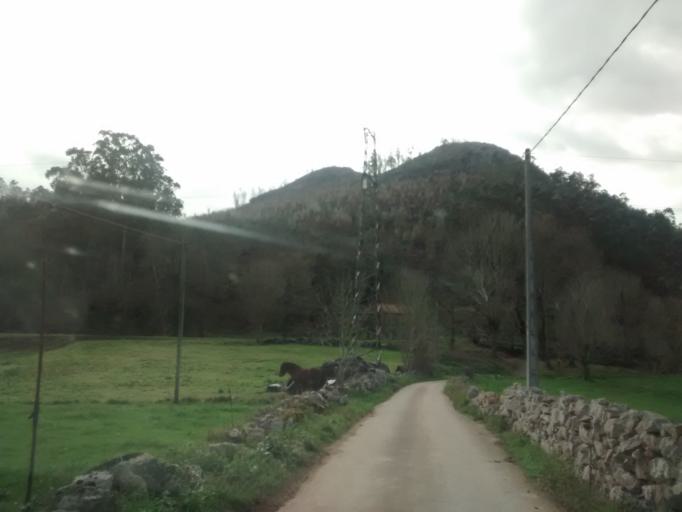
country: ES
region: Cantabria
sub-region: Provincia de Cantabria
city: Entrambasaguas
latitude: 43.3422
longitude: -3.6996
